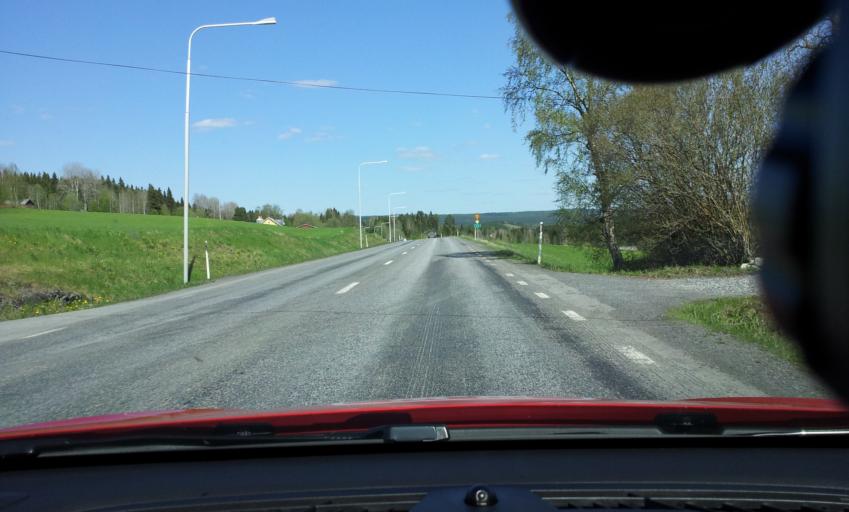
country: SE
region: Jaemtland
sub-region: Are Kommun
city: Jarpen
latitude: 63.3293
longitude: 13.4008
